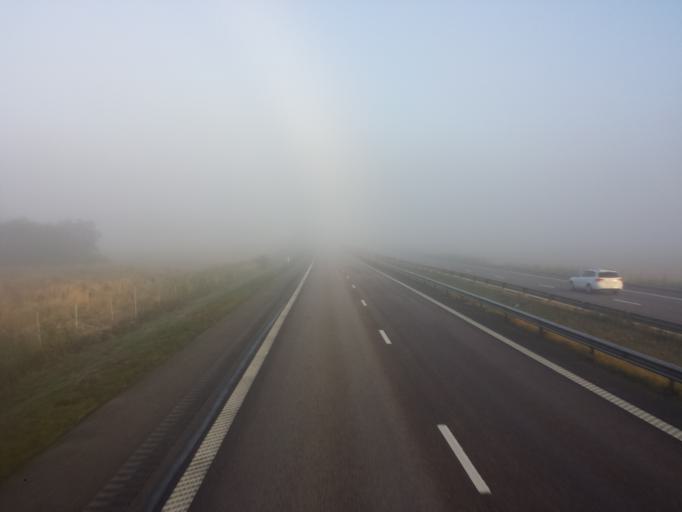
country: SE
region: Halland
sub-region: Kungsbacka Kommun
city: Kungsbacka
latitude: 57.4529
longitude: 12.0928
